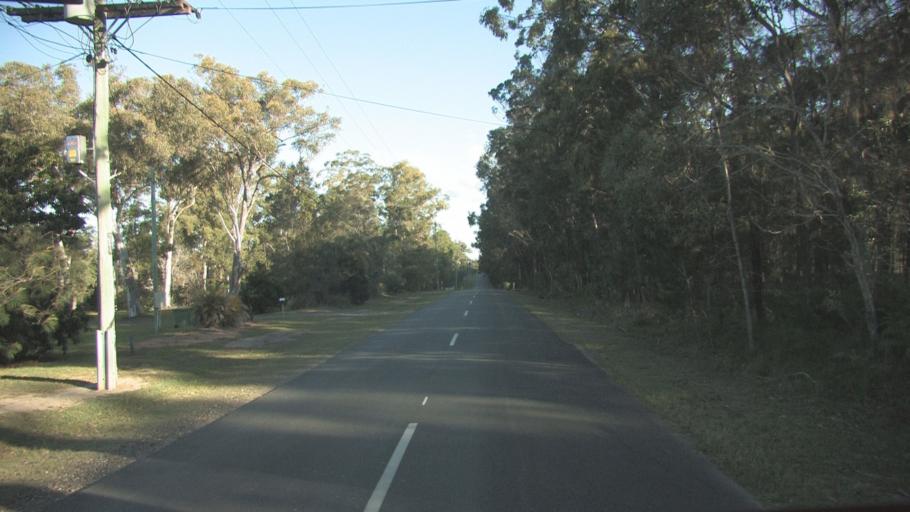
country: AU
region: Queensland
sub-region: Gold Coast
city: Yatala
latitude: -27.6795
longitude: 153.2753
